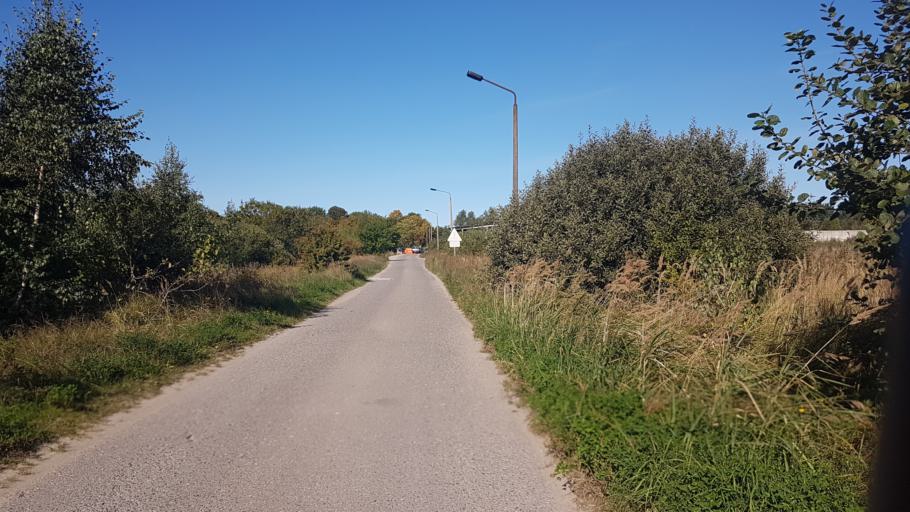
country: DE
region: Mecklenburg-Vorpommern
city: Sagard
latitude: 54.5005
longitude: 13.5388
